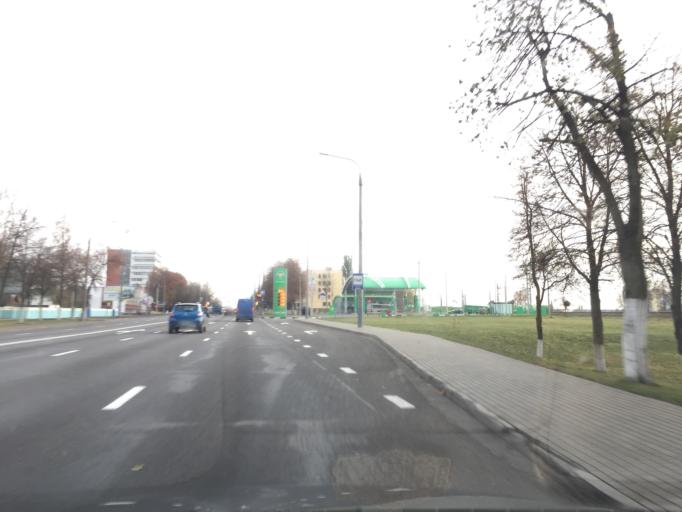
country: BY
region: Gomel
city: Gomel
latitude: 52.4755
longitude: 30.9760
